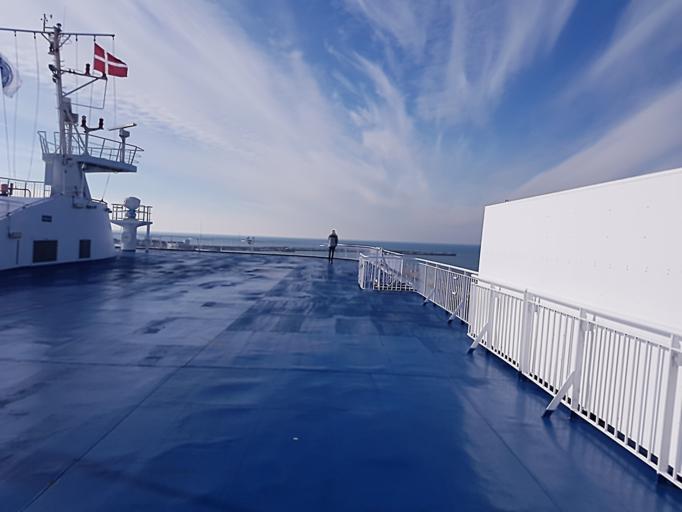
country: DK
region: North Denmark
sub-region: Hjorring Kommune
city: Hirtshals
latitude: 57.5960
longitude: 9.9738
